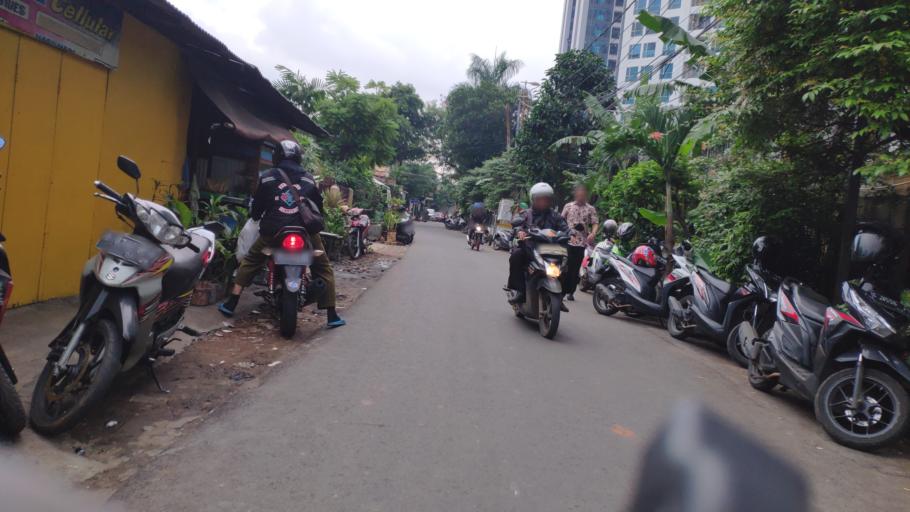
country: ID
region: Jakarta Raya
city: Jakarta
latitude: -6.2241
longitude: 106.8414
